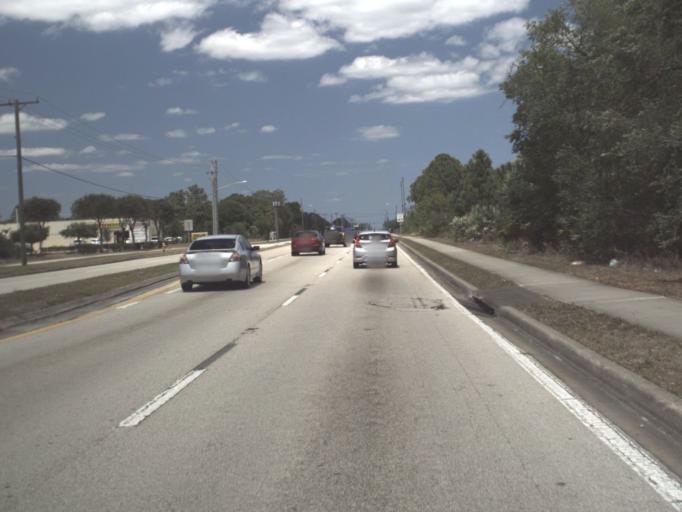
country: US
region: Florida
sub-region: Brevard County
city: Palm Bay
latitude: 28.0434
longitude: -80.6215
